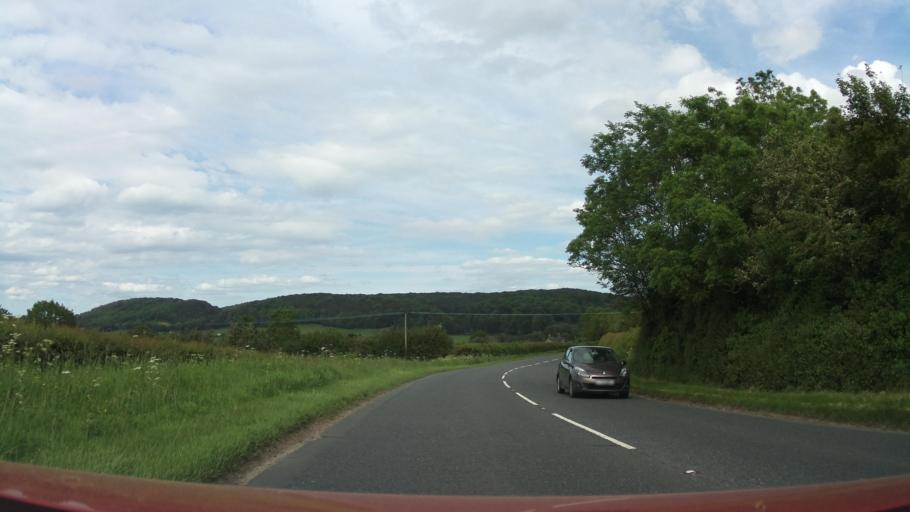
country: GB
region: England
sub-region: Herefordshire
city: Evesbatch
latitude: 52.1267
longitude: -2.3996
